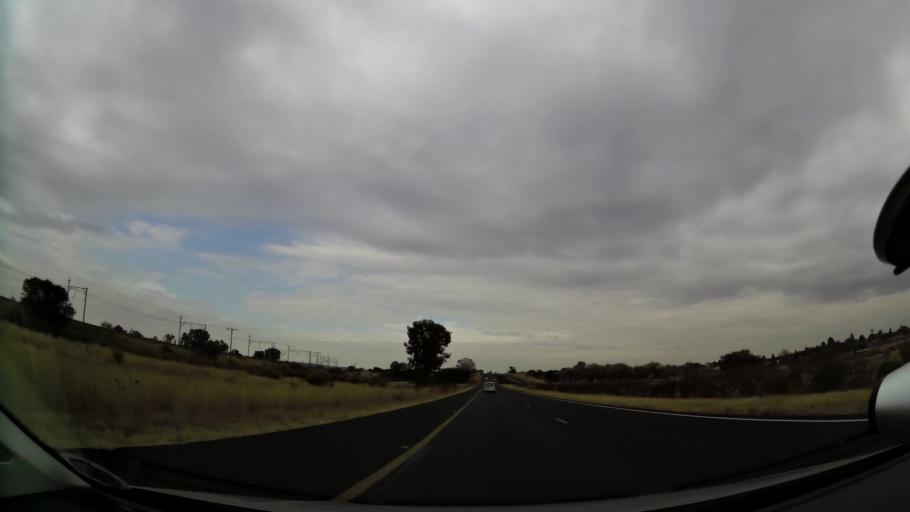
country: ZA
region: Orange Free State
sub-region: Fezile Dabi District Municipality
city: Kroonstad
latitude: -27.6319
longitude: 27.2505
